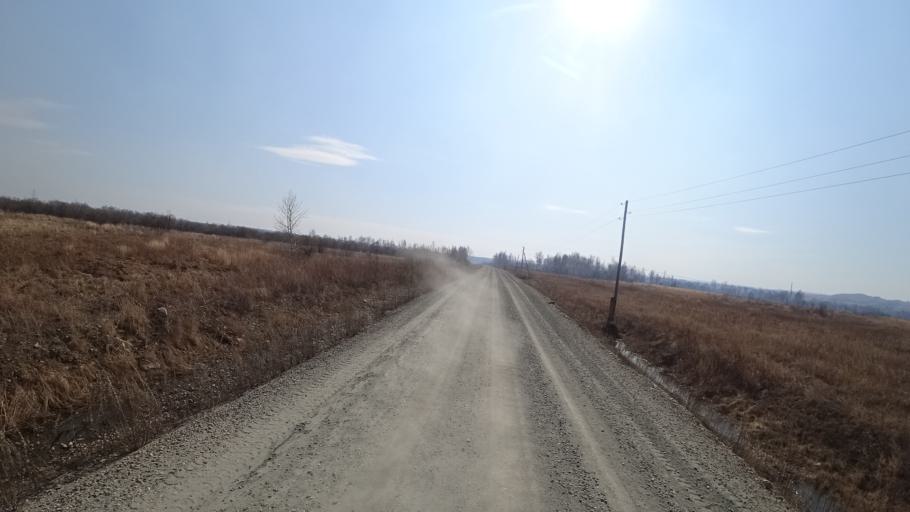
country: RU
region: Amur
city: Novobureyskiy
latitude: 49.8073
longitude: 129.9657
